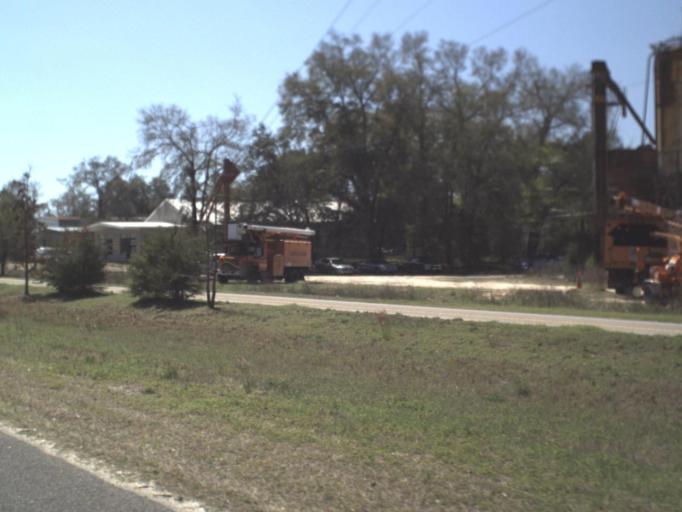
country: US
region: Florida
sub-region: Leon County
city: Tallahassee
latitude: 30.3867
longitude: -84.2750
